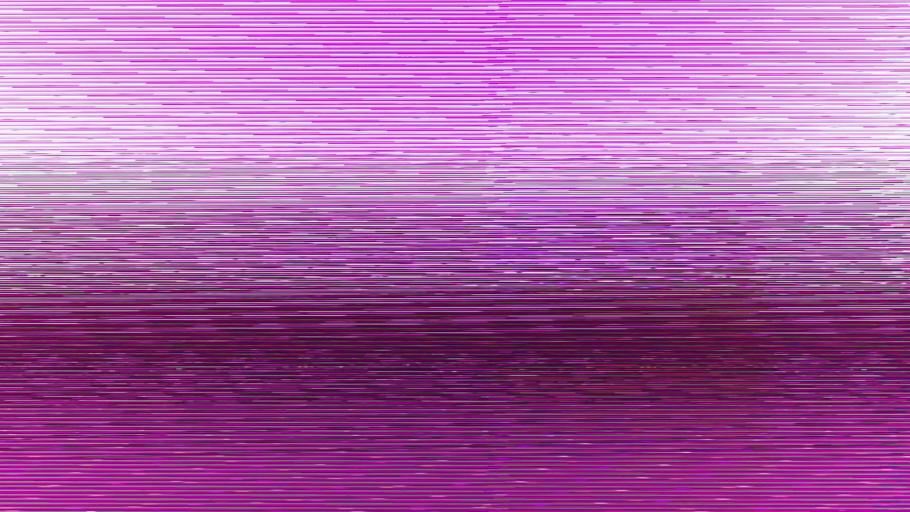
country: US
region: Michigan
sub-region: Washtenaw County
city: Ypsilanti
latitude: 42.2252
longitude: -83.6329
